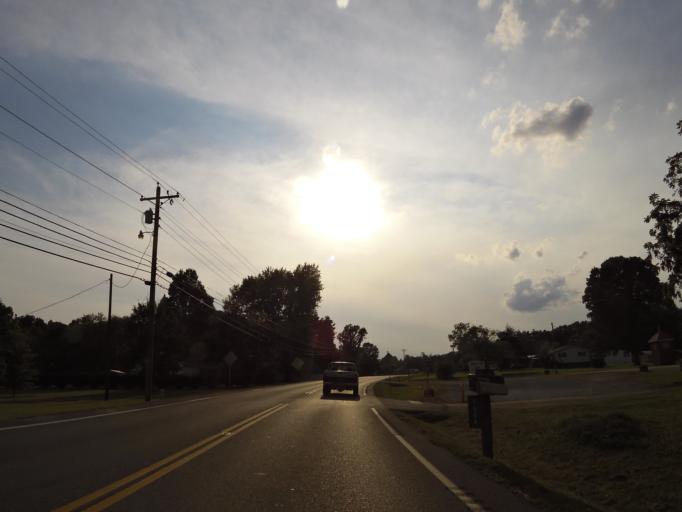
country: US
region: Tennessee
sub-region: Morgan County
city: Coalfield
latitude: 36.0336
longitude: -84.4162
